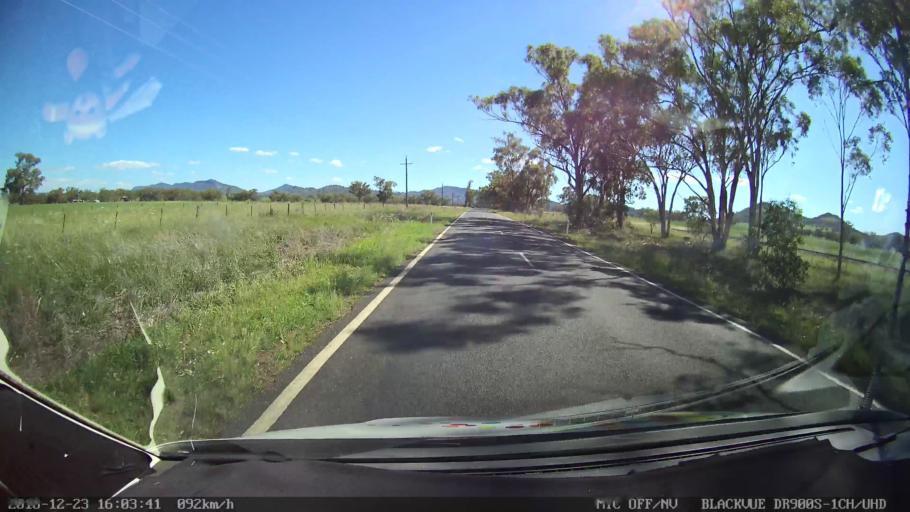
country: AU
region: New South Wales
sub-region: Tamworth Municipality
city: Phillip
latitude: -31.2464
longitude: 150.7985
